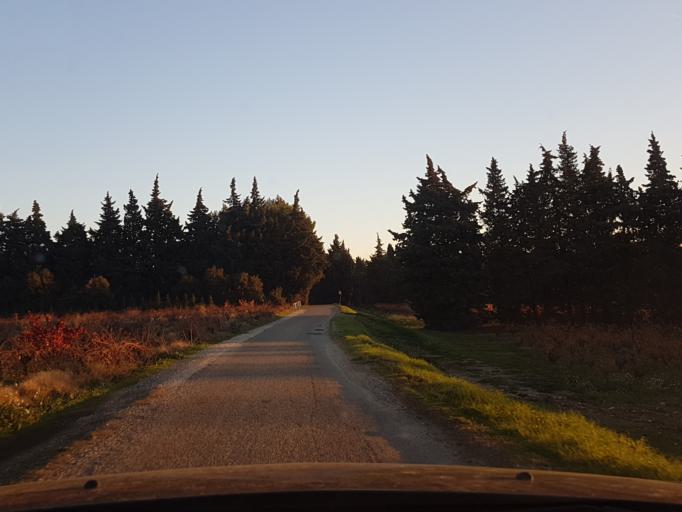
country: FR
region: Provence-Alpes-Cote d'Azur
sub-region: Departement du Vaucluse
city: Saint-Saturnin-les-Avignon
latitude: 43.9587
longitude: 4.9147
